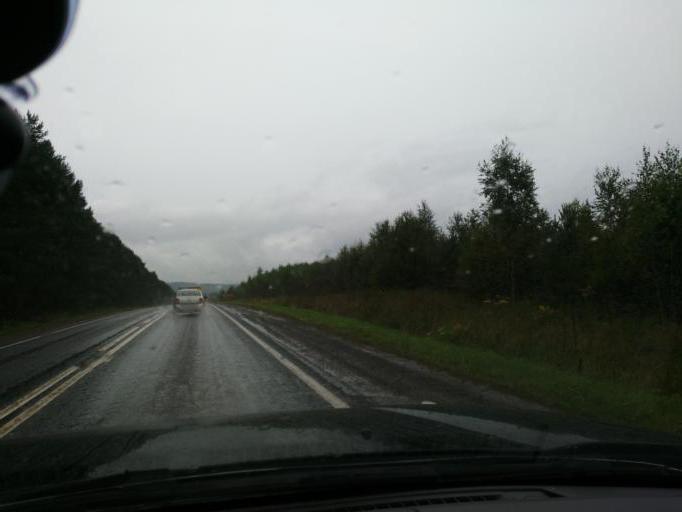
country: RU
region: Perm
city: Yugo-Kamskiy
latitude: 57.6764
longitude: 55.5792
